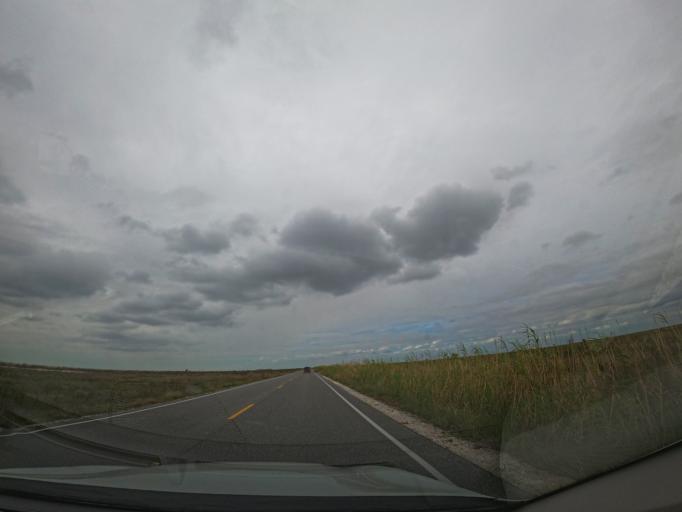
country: US
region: Louisiana
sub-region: Cameron Parish
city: Cameron
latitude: 29.7665
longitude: -93.3754
